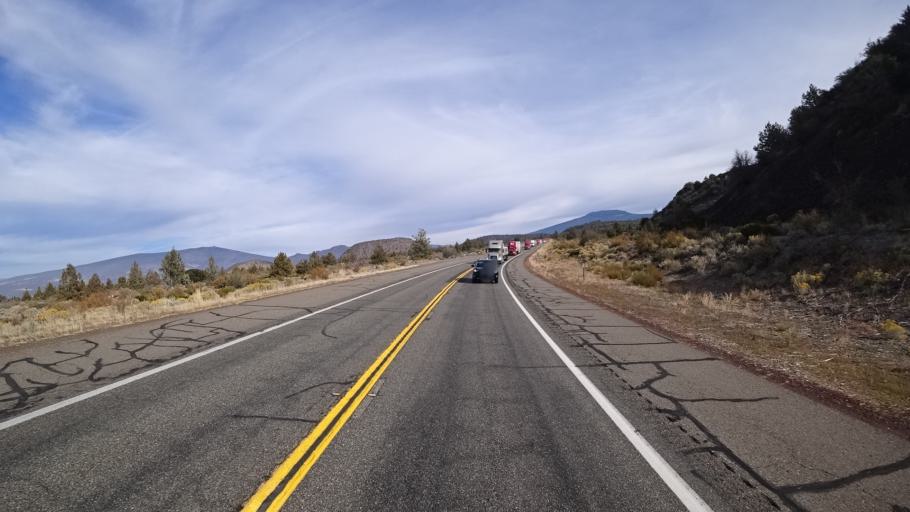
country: US
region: California
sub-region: Siskiyou County
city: Weed
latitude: 41.5205
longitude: -122.3049
